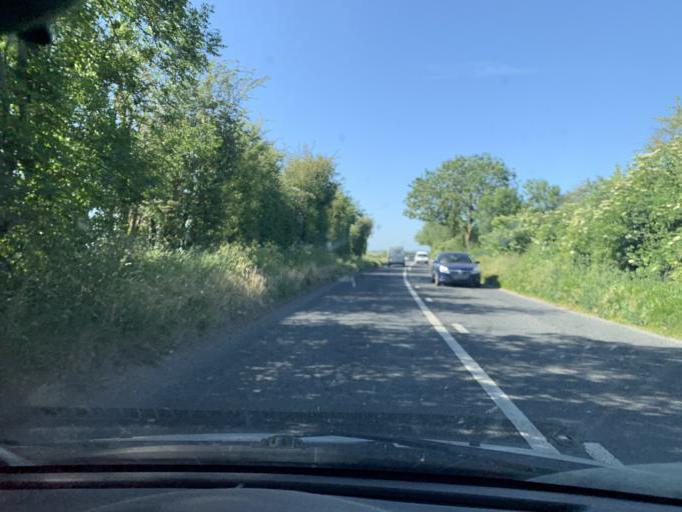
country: GB
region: England
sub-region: Wiltshire
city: Durnford
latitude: 51.1206
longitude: -1.7881
